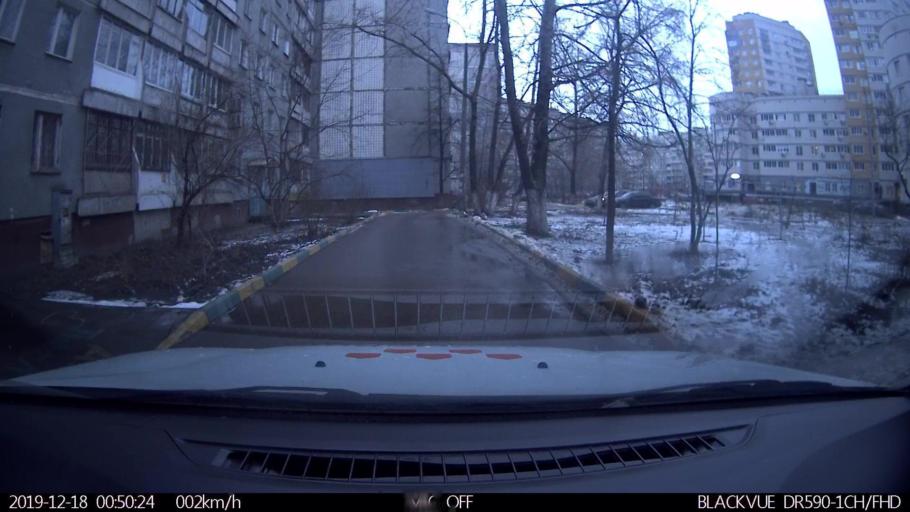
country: RU
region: Nizjnij Novgorod
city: Nizhniy Novgorod
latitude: 56.3410
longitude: 43.9242
